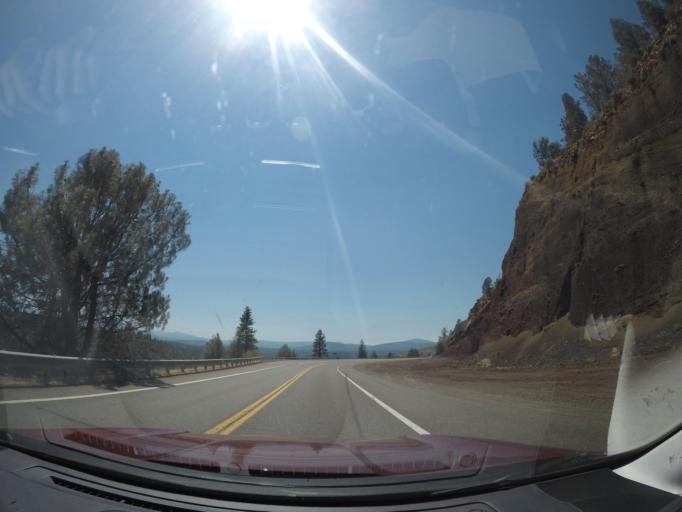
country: US
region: California
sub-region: Shasta County
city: Burney
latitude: 40.9929
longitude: -121.4820
